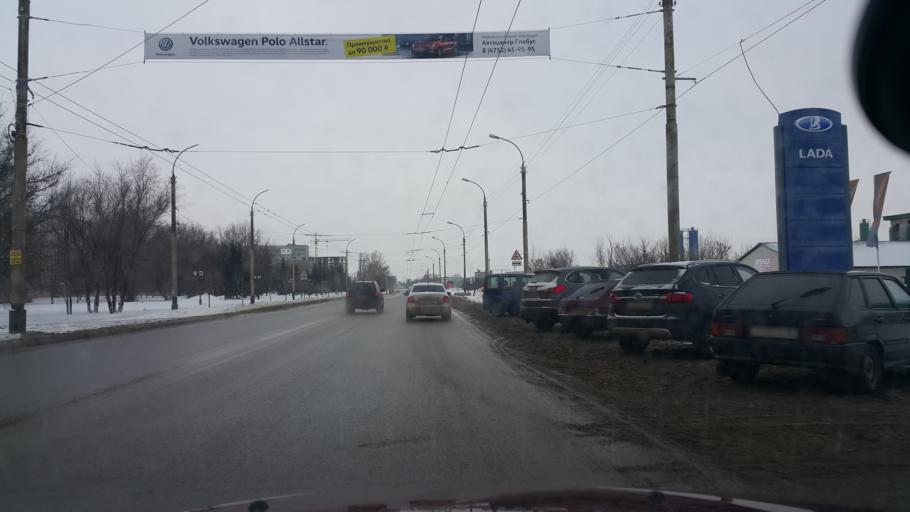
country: RU
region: Tambov
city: Tambov
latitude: 52.7364
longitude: 41.3864
